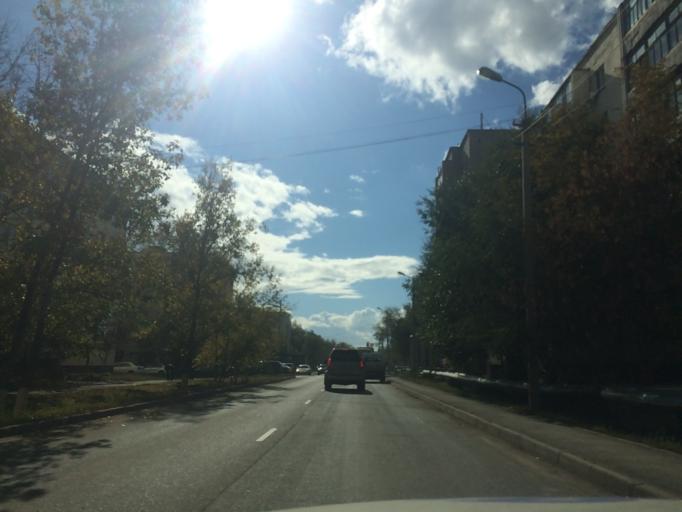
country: KZ
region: Astana Qalasy
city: Astana
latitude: 51.1976
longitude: 71.3921
